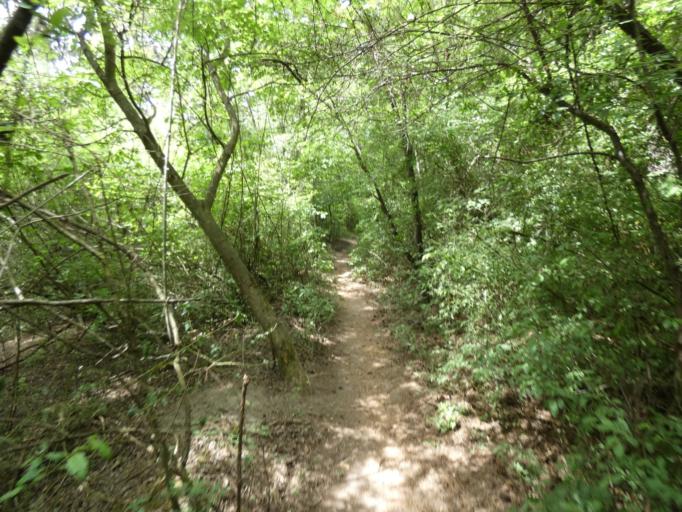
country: HU
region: Pest
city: Pilisborosjeno
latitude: 47.6109
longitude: 19.0005
